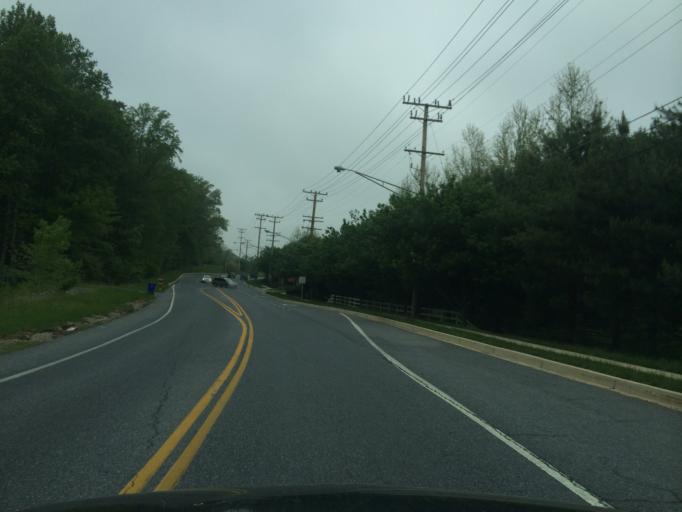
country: US
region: Maryland
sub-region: Howard County
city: Riverside
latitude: 39.1788
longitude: -76.8982
